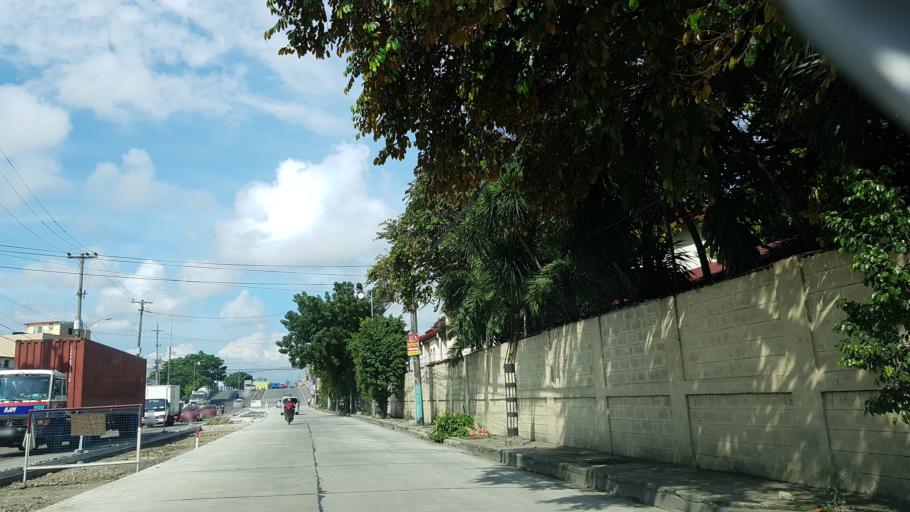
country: PH
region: Metro Manila
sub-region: San Juan
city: San Juan
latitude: 14.5848
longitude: 121.0181
